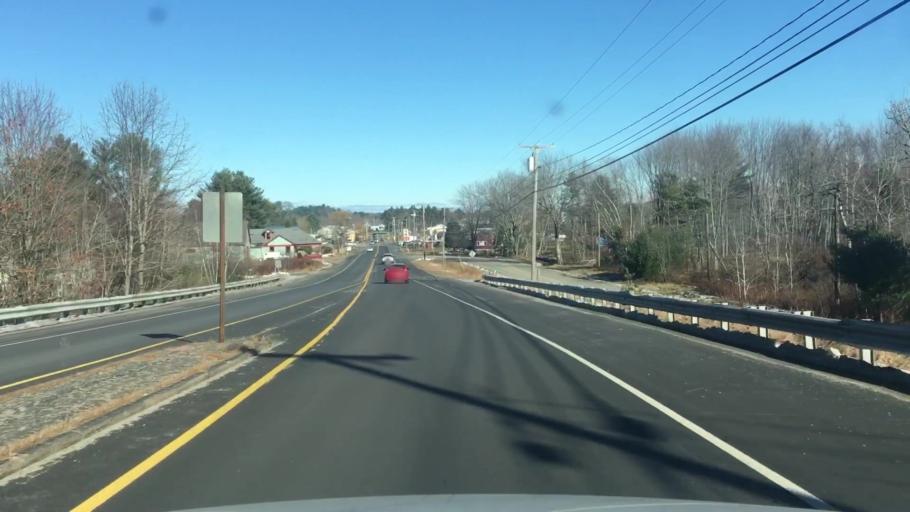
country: US
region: Maine
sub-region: York County
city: Biddeford
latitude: 43.4571
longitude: -70.4933
